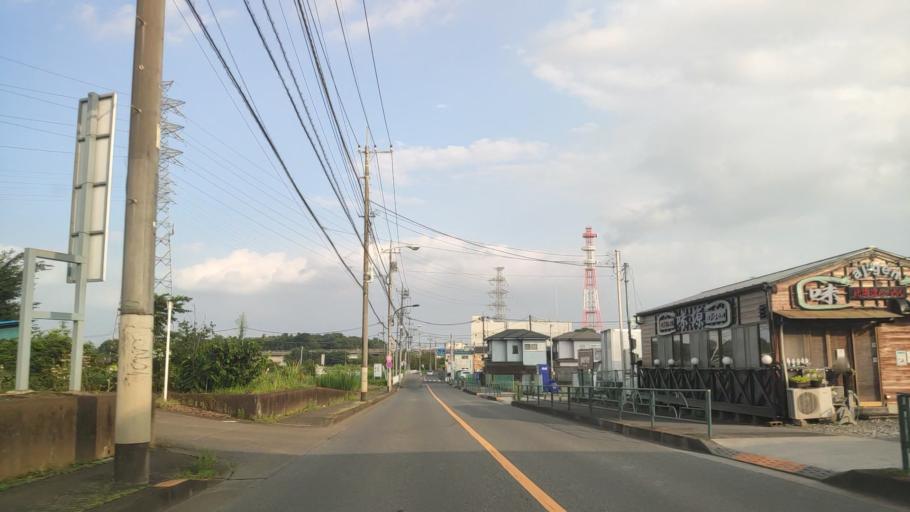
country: JP
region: Saitama
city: Hanno
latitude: 35.7984
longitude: 139.3148
